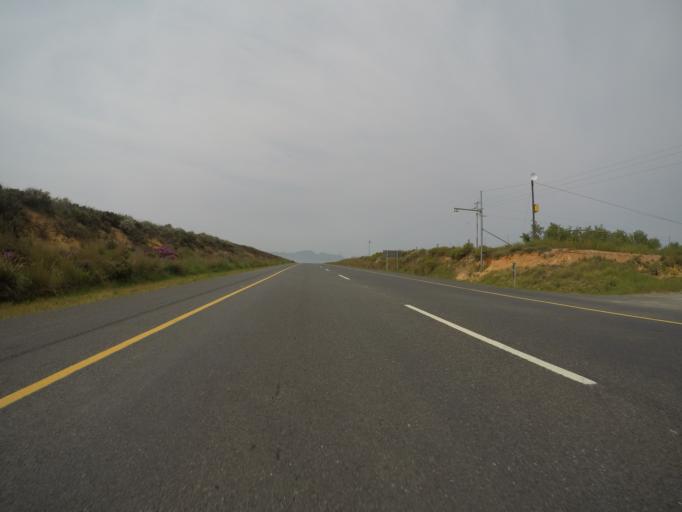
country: ZA
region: Western Cape
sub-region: Cape Winelands District Municipality
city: Noorder-Paarl
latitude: -33.5589
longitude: 18.8774
